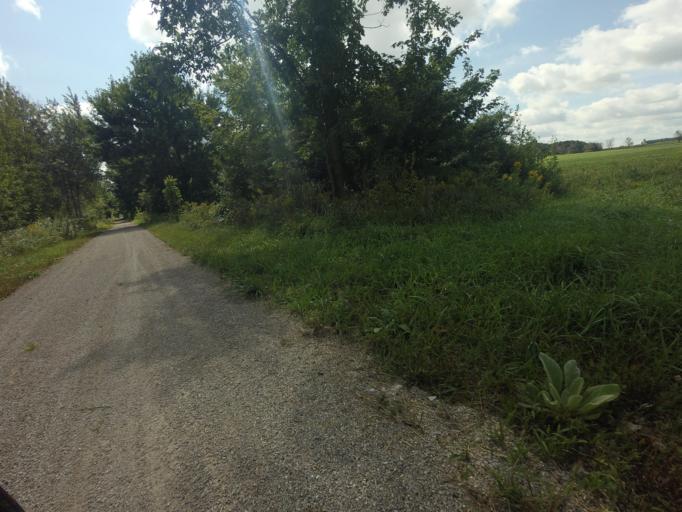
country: CA
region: Ontario
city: Huron East
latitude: 43.6484
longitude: -81.2224
